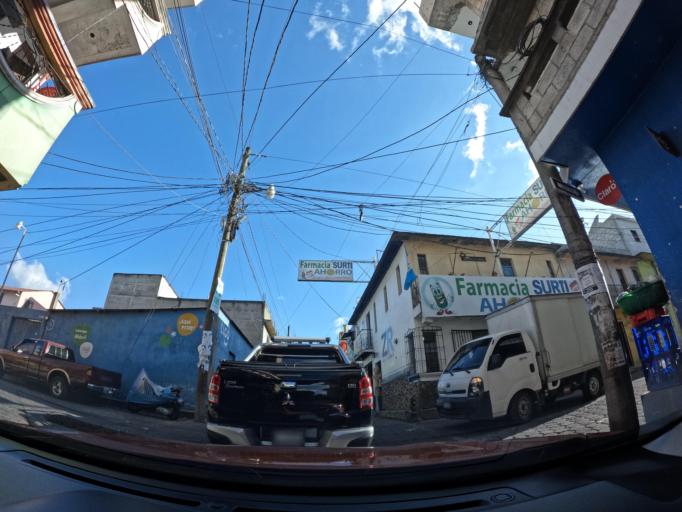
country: GT
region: Sacatepequez
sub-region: Municipio de Santa Maria de Jesus
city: Santa Maria de Jesus
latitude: 14.4949
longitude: -90.7092
